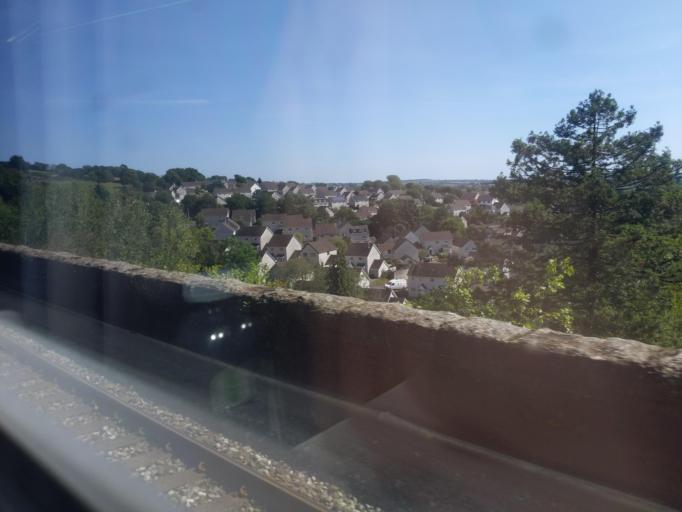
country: GB
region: England
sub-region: Devon
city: Ivybridge
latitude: 50.3965
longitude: -3.9207
